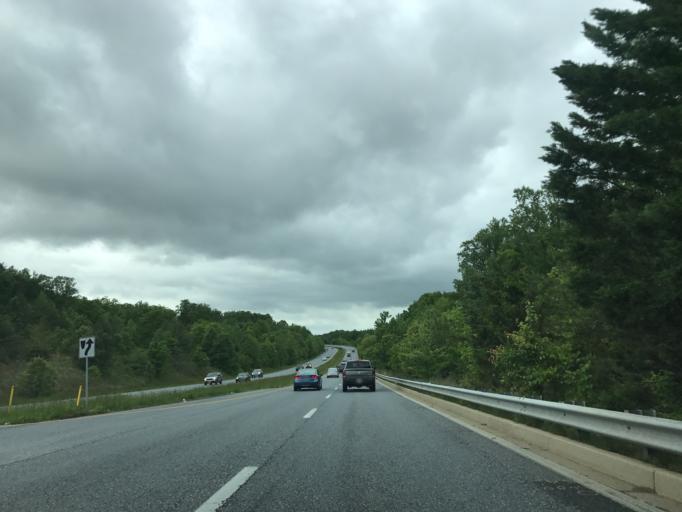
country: US
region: Maryland
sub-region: Prince George's County
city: Woodlawn
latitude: 38.9552
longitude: -76.8889
